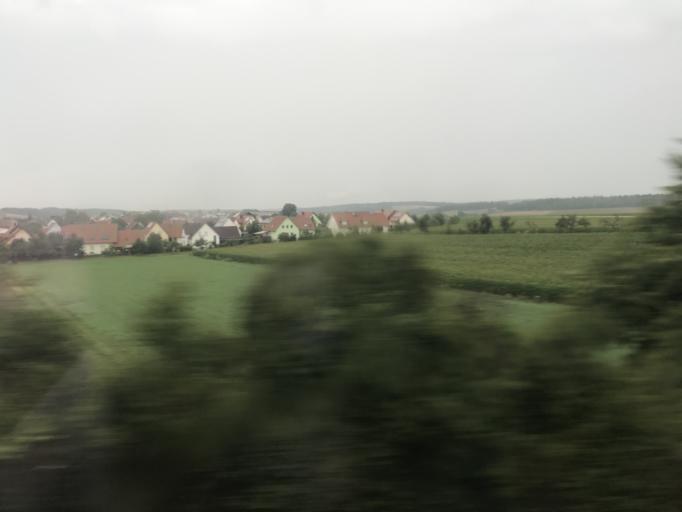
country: DE
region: Bavaria
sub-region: Regierungsbezirk Unterfranken
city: Werneck
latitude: 49.9457
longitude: 10.0868
